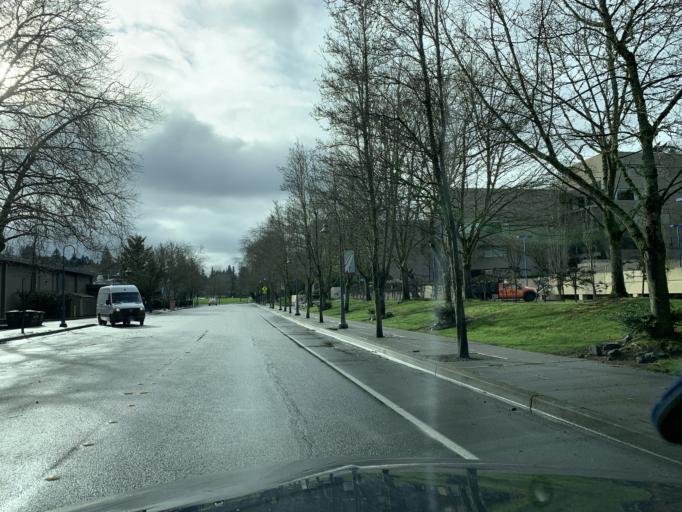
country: US
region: Washington
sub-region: King County
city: Mercer Island
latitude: 47.5834
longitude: -122.2351
